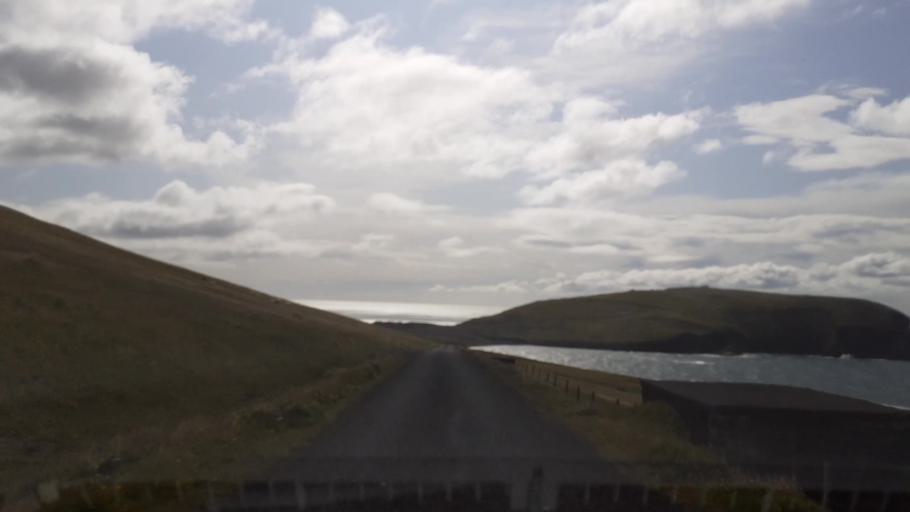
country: IS
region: South
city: Vestmannaeyjar
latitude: 63.4153
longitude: -20.2808
